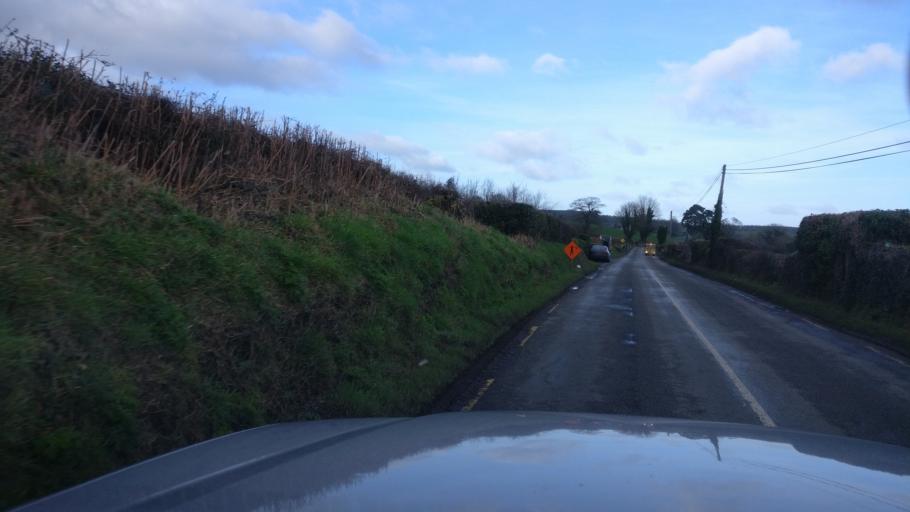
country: IE
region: Leinster
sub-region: Kilkenny
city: Castlecomer
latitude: 52.8189
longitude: -7.2126
